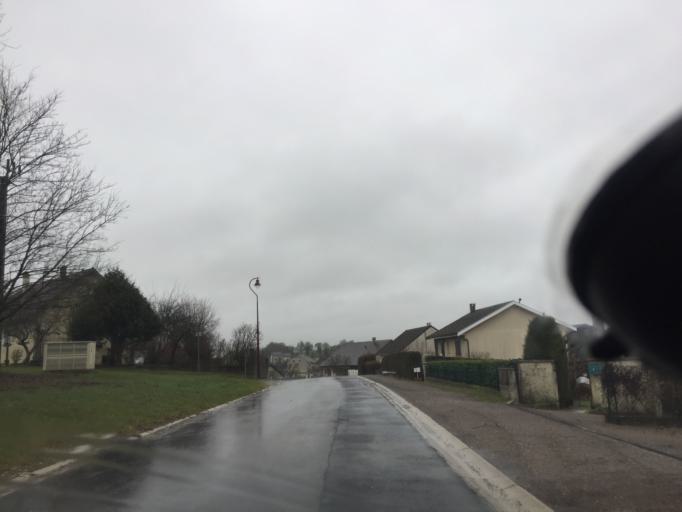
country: FR
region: Franche-Comte
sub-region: Departement du Jura
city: Orchamps
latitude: 47.1506
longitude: 5.6057
